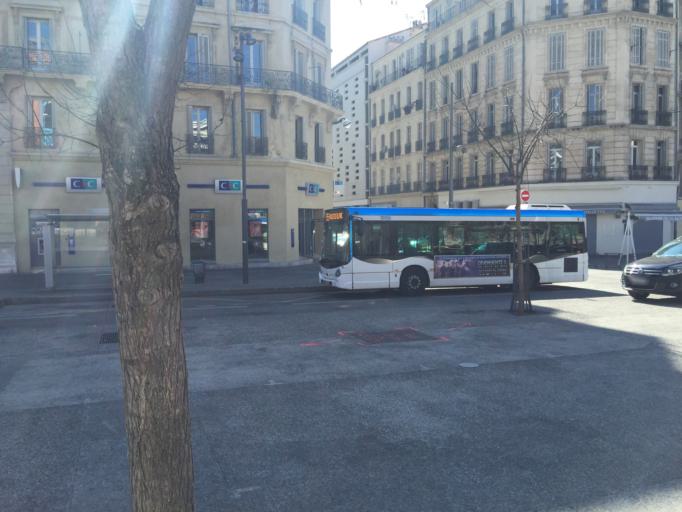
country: FR
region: Provence-Alpes-Cote d'Azur
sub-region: Departement des Bouches-du-Rhone
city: Marseille 02
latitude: 43.3048
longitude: 5.3667
